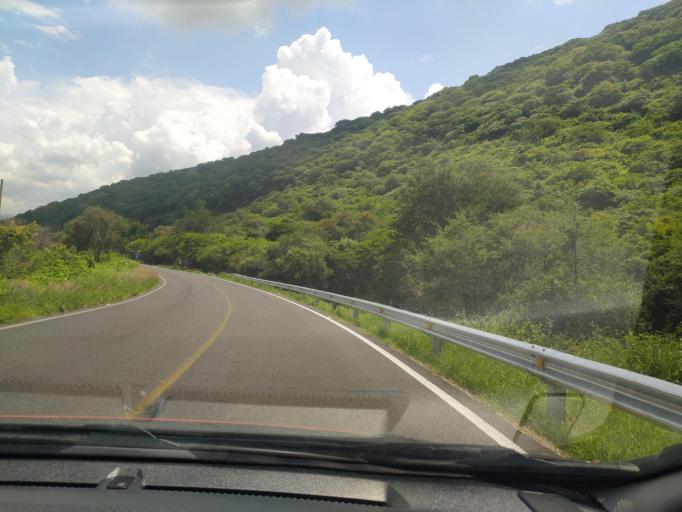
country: MX
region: Jalisco
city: Villa Corona
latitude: 20.3689
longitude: -103.6700
